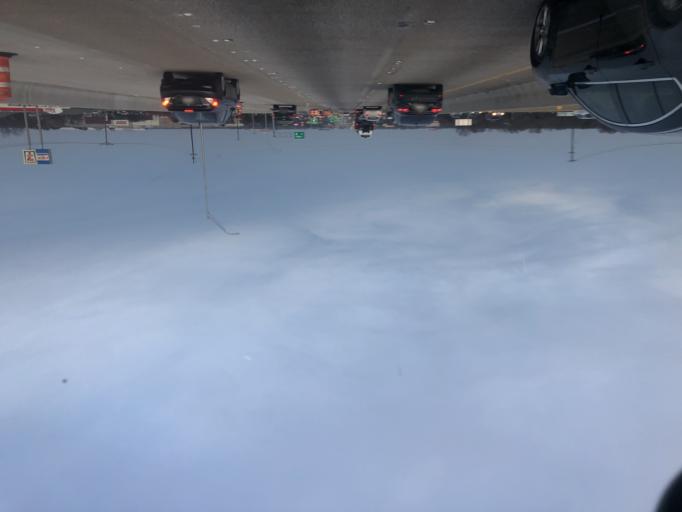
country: US
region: Texas
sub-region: Dallas County
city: Shamrock
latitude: 32.6189
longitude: -96.9145
